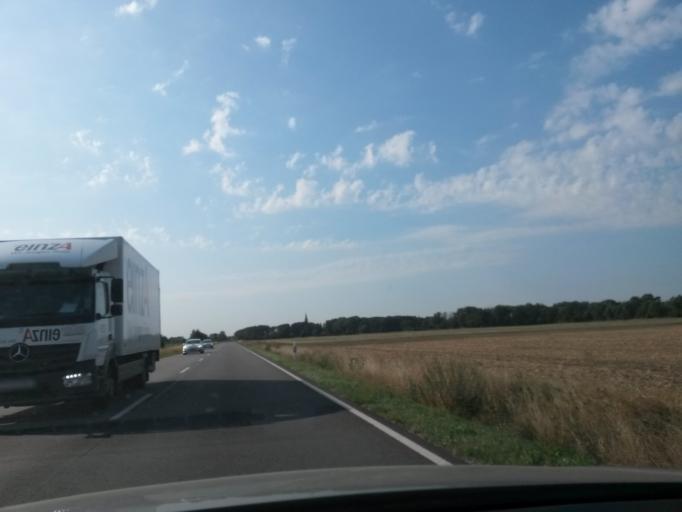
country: DE
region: Saxony-Anhalt
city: Jerichow
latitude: 52.5149
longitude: 12.0160
